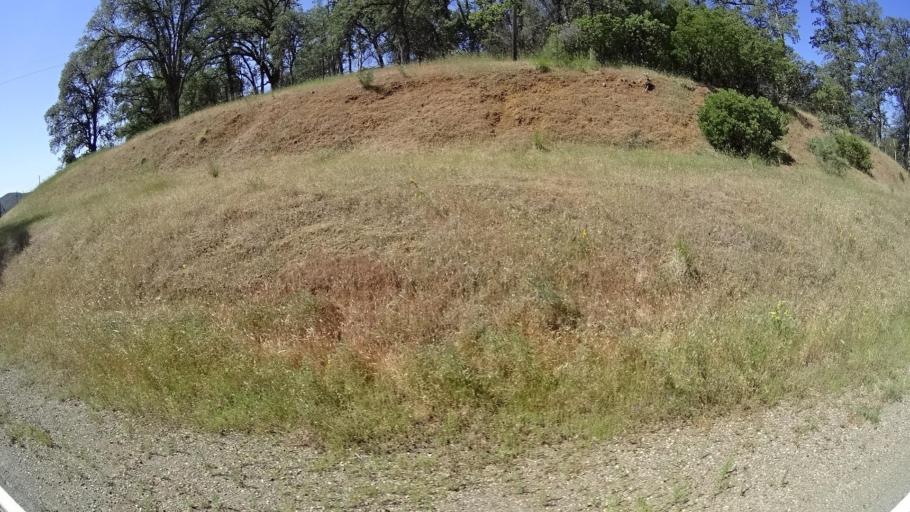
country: US
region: California
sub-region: Lake County
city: Hidden Valley Lake
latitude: 38.8752
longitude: -122.4226
